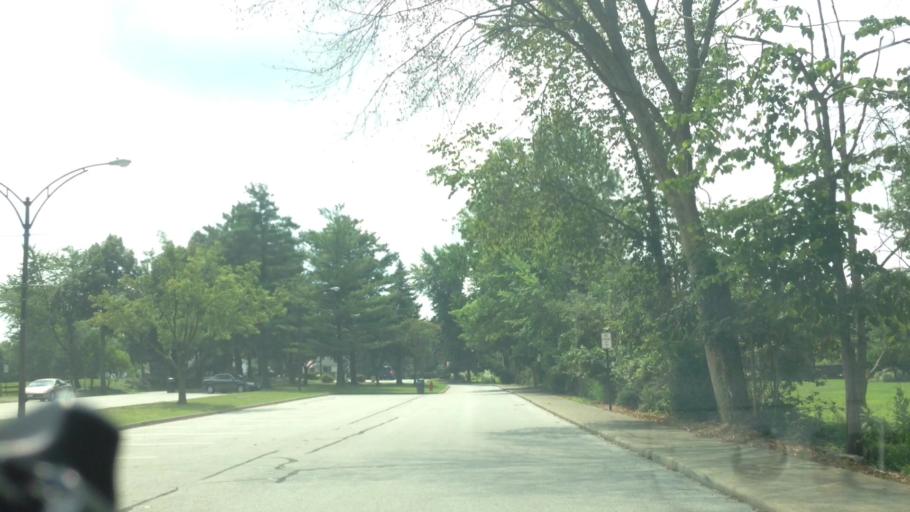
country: US
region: Ohio
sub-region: Cuyahoga County
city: Highland Heights
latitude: 41.5404
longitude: -81.4666
